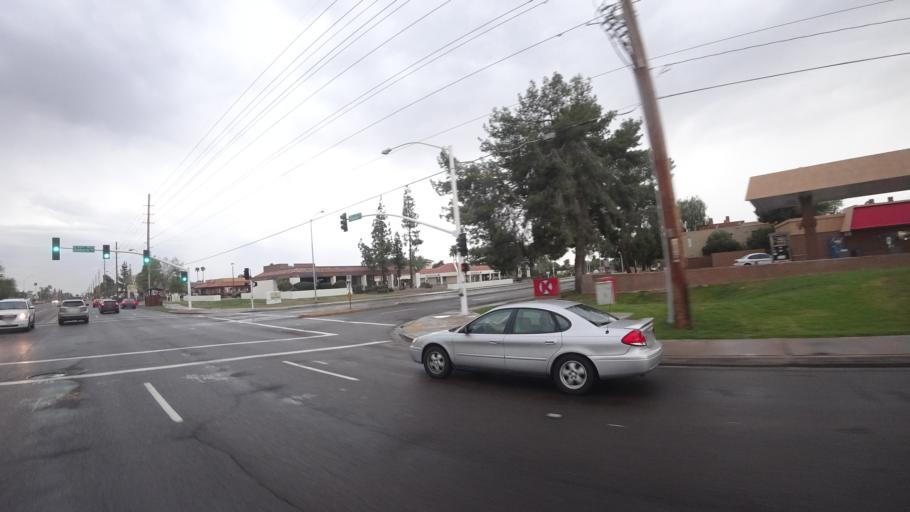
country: US
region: Arizona
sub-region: Maricopa County
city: Scottsdale
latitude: 33.4879
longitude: -111.9090
